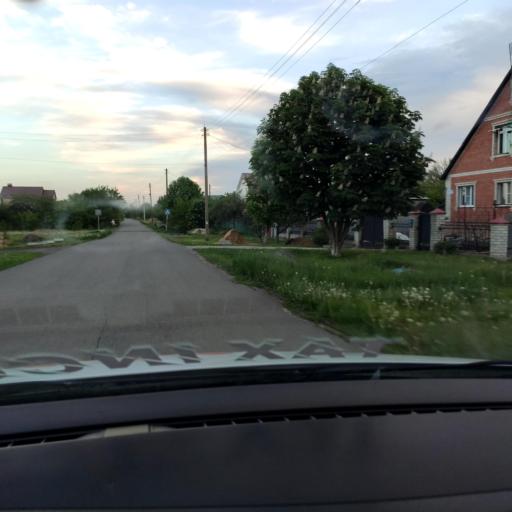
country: RU
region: Voronezj
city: Maslovka
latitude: 51.4454
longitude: 39.2346
